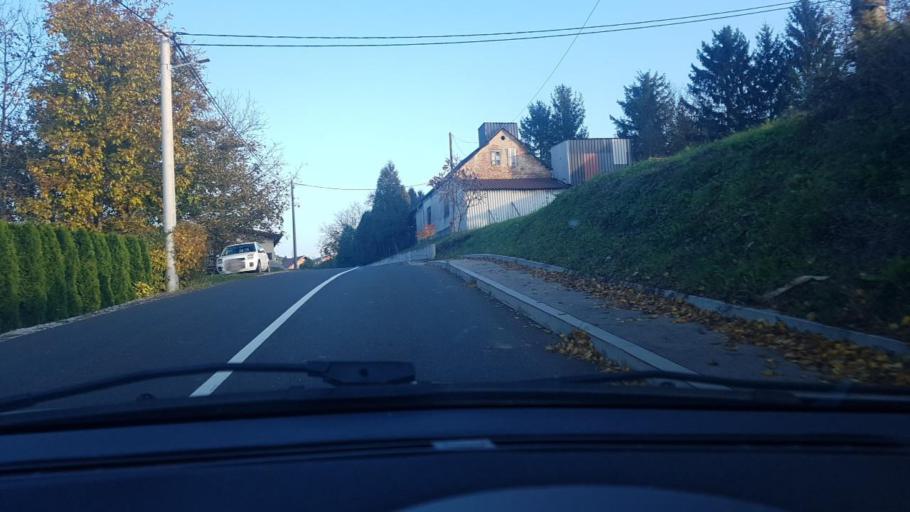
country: SI
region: Rogaska Slatina
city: Rogaska Slatina
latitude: 46.2147
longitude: 15.6651
